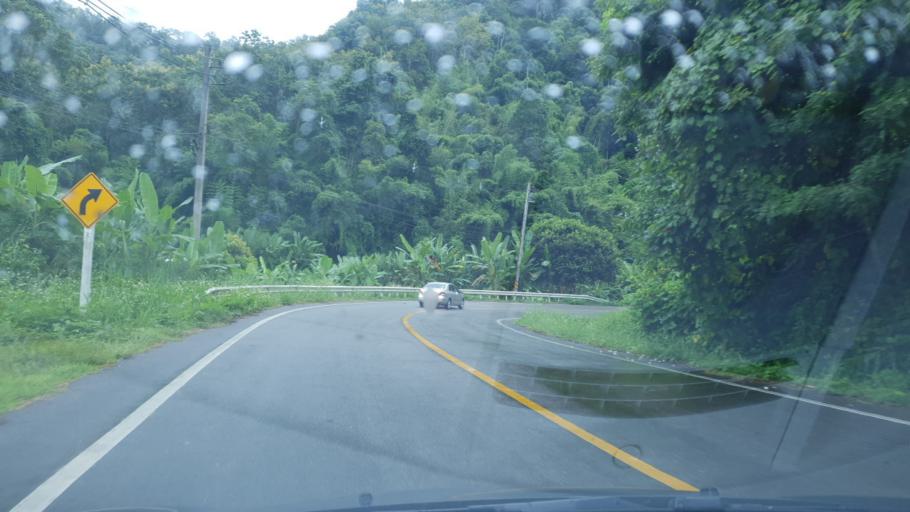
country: TH
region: Mae Hong Son
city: Mae La Noi
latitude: 18.5727
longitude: 97.9351
